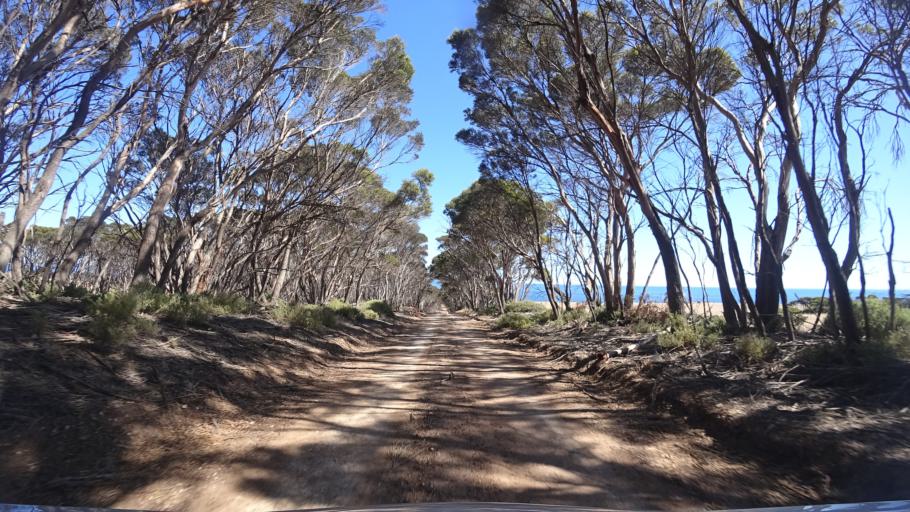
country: AU
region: South Australia
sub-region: Kangaroo Island
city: Kingscote
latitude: -35.7416
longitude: 137.7212
